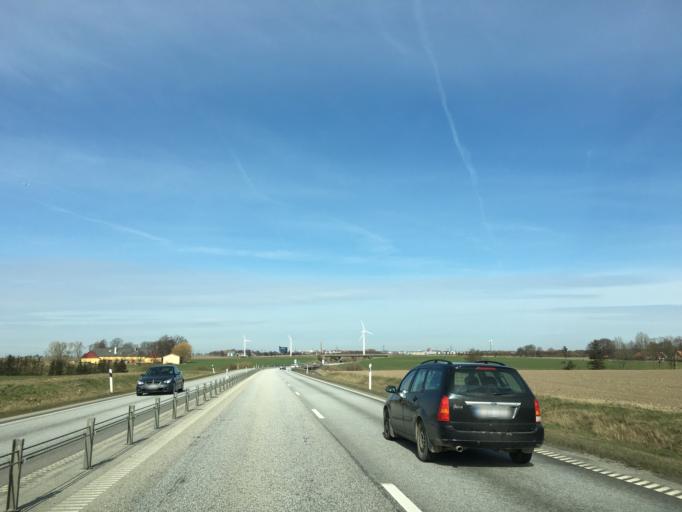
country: SE
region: Skane
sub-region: Staffanstorps Kommun
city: Hjaerup
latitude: 55.7010
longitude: 13.1377
